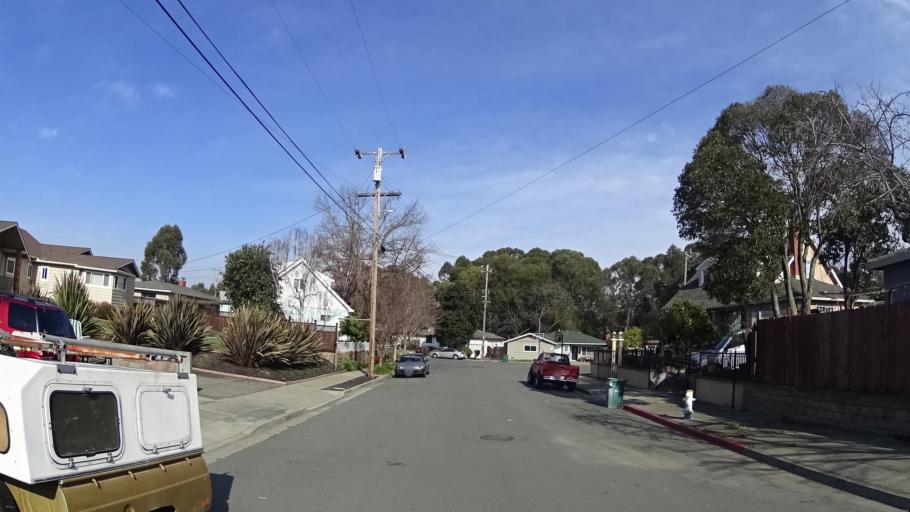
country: US
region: California
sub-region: Alameda County
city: Fairview
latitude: 37.6745
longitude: -122.0606
